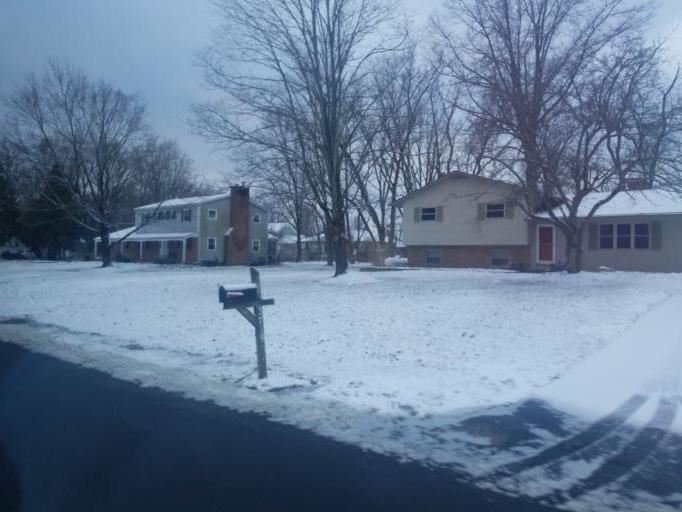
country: US
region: Ohio
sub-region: Franklin County
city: Gahanna
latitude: 40.0501
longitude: -82.8444
